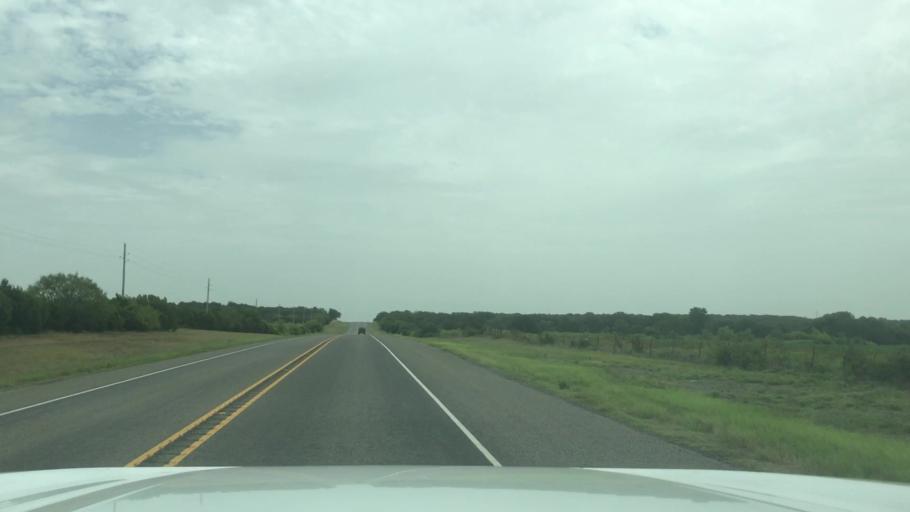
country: US
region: Texas
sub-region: Hamilton County
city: Hico
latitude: 31.9817
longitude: -98.0012
